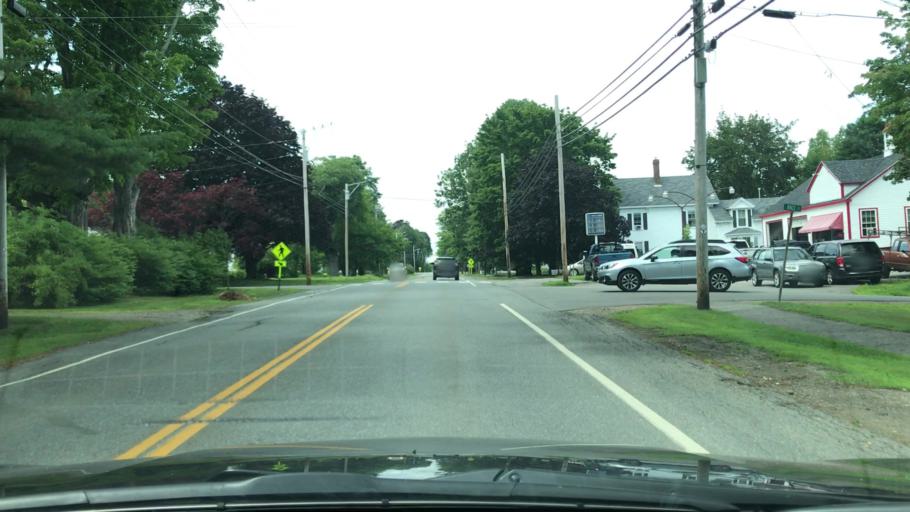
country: US
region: Maine
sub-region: Waldo County
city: Belfast
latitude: 44.4177
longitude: -68.9980
